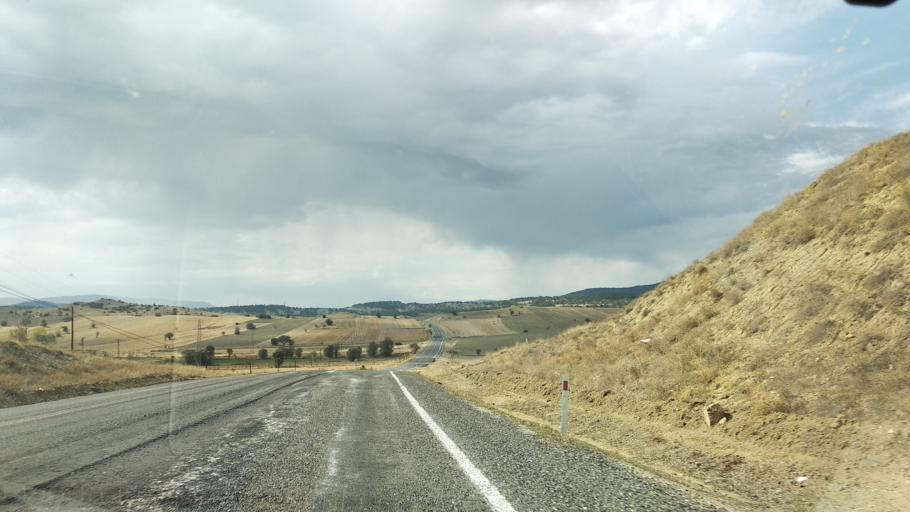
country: TR
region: Bolu
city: Seben
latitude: 40.3712
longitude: 31.5090
